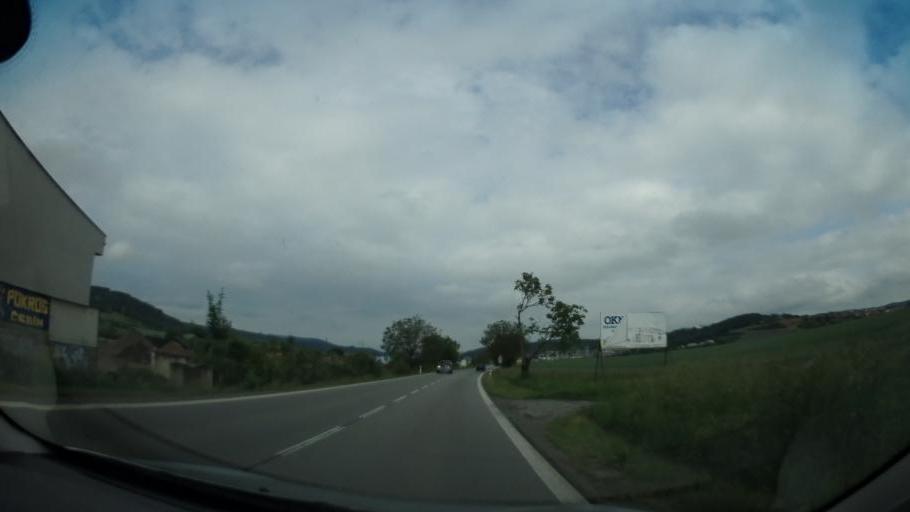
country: CZ
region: South Moravian
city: Cebin
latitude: 49.3200
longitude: 16.4676
